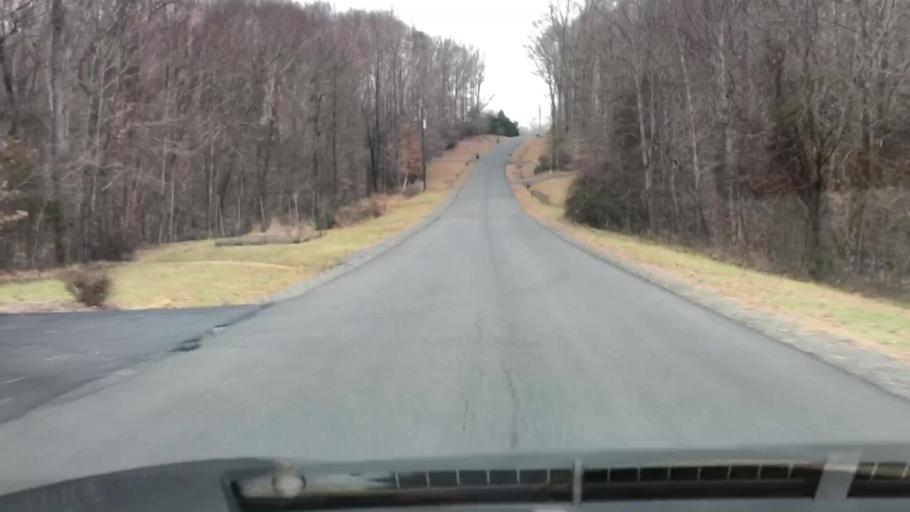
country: US
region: Virginia
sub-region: Stafford County
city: Falmouth
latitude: 38.3868
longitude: -77.5991
